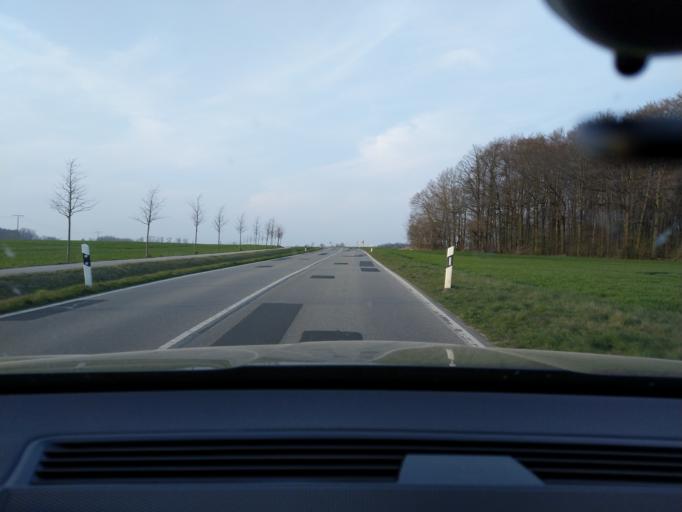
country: DE
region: Mecklenburg-Vorpommern
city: Kramerhof
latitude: 54.3398
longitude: 13.0306
